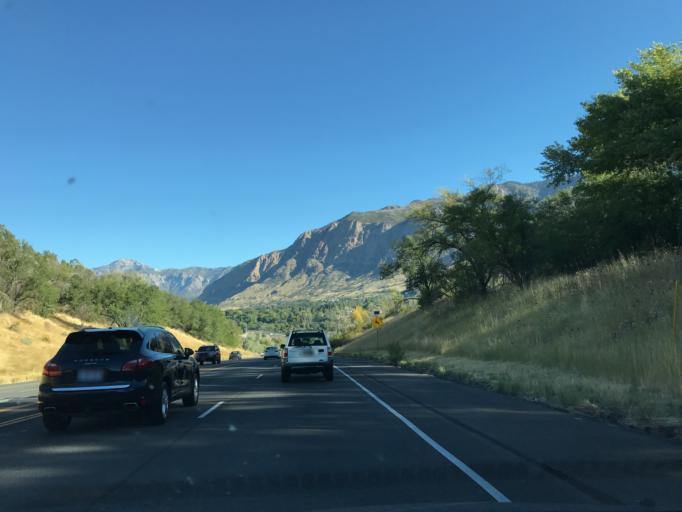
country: US
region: Utah
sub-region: Weber County
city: Ogden
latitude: 41.2322
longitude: -111.9475
